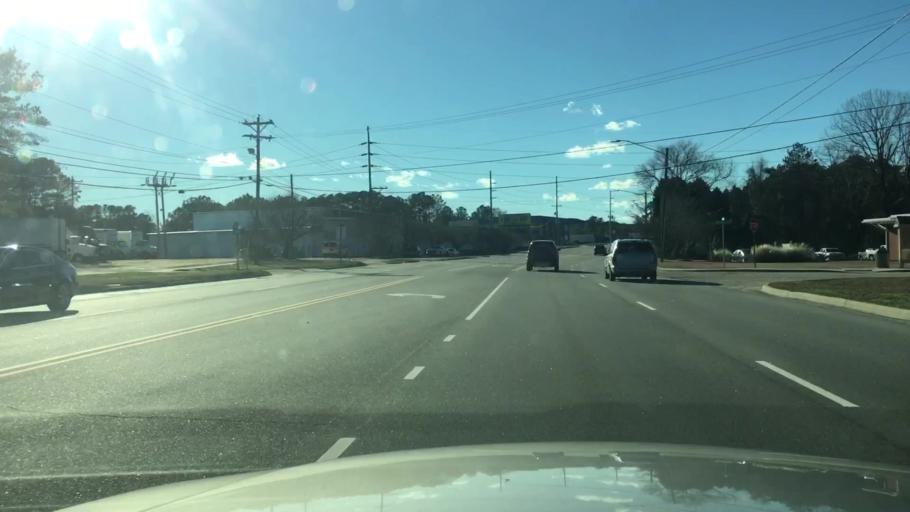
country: US
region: North Carolina
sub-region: Cumberland County
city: Fayetteville
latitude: 35.0406
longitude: -78.9017
